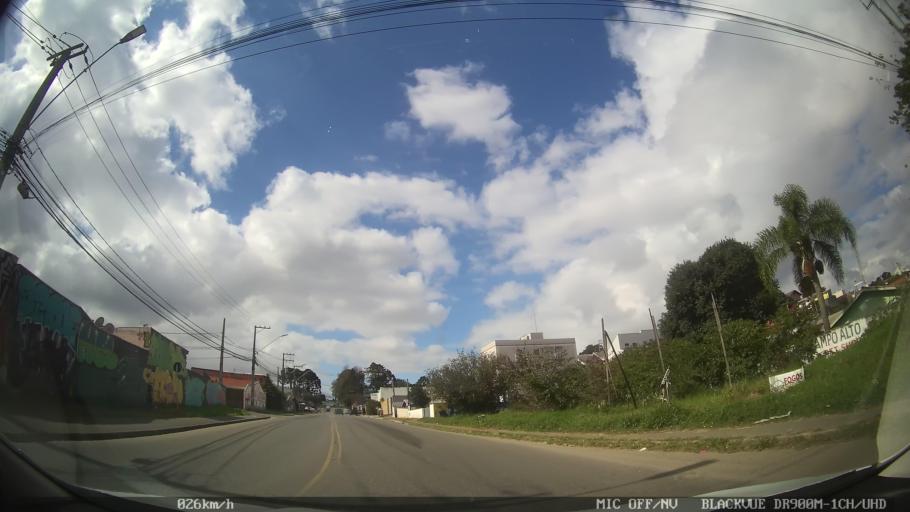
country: BR
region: Parana
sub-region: Pinhais
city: Pinhais
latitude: -25.3728
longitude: -49.2048
